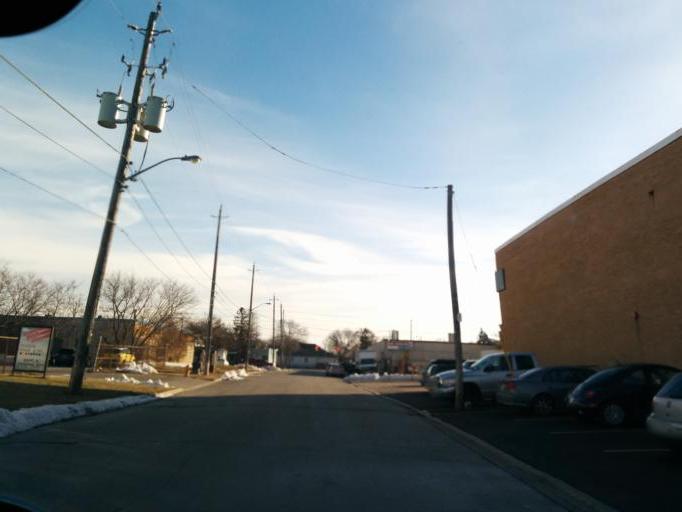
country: CA
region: Ontario
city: Etobicoke
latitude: 43.6140
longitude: -79.5409
